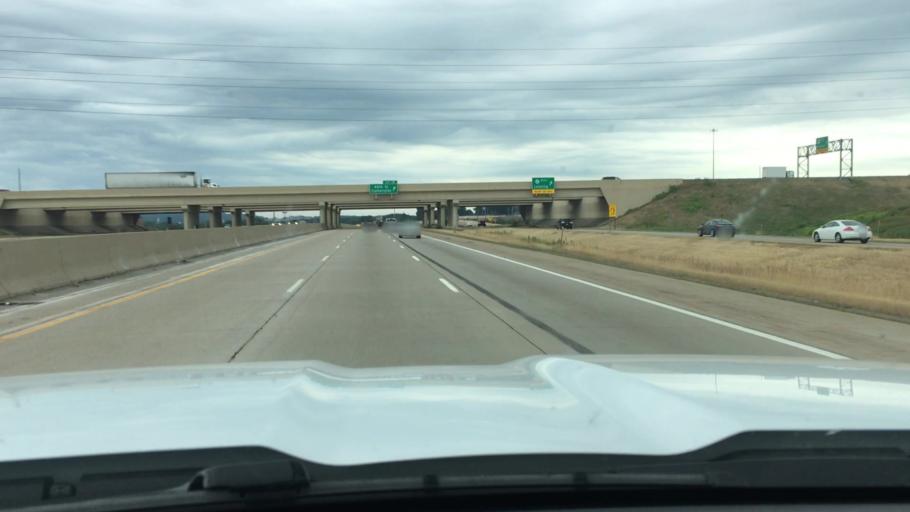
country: US
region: Michigan
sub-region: Kent County
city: Cutlerville
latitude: 42.8507
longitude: -85.6788
